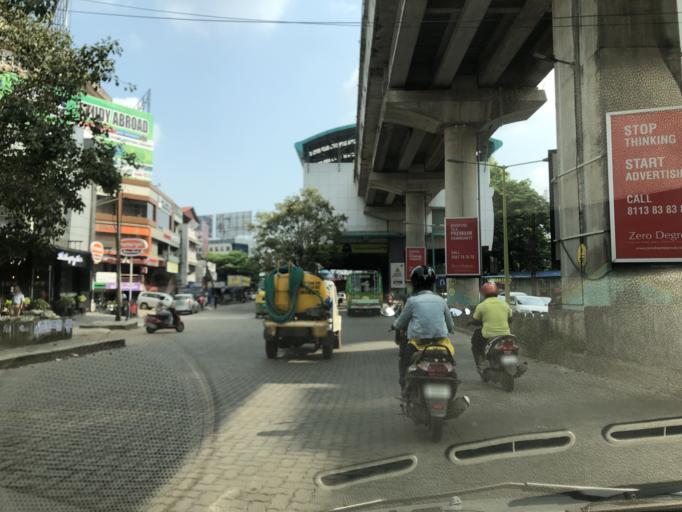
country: IN
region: Kerala
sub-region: Ernakulam
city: Cochin
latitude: 9.9936
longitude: 76.2907
